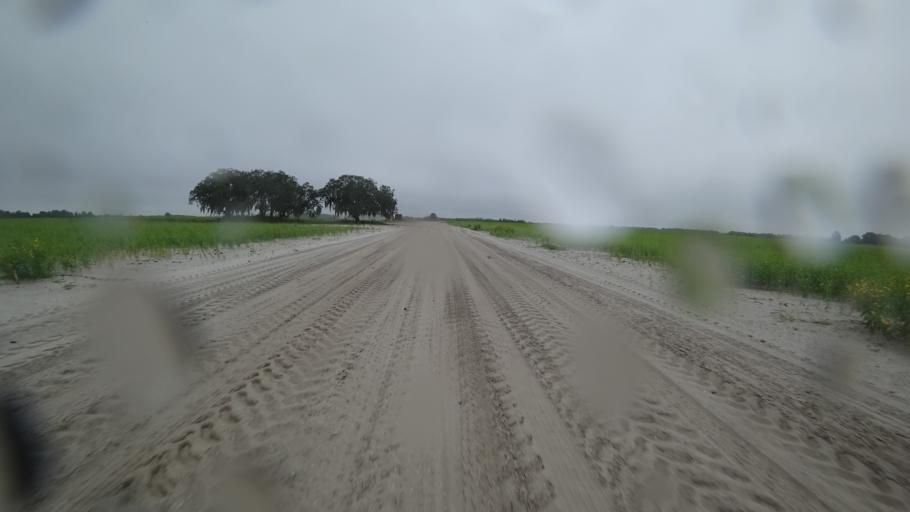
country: US
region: Florida
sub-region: Sarasota County
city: Warm Mineral Springs
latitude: 27.2924
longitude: -82.1605
